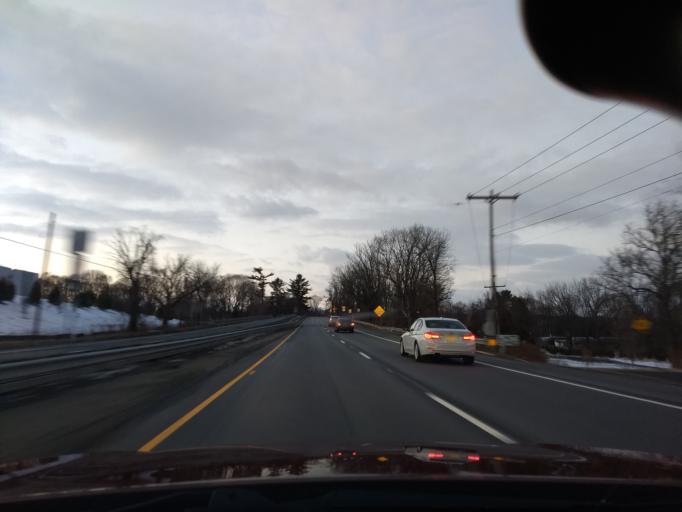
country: US
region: New Jersey
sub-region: Warren County
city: Phillipsburg
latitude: 40.6970
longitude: -75.1624
